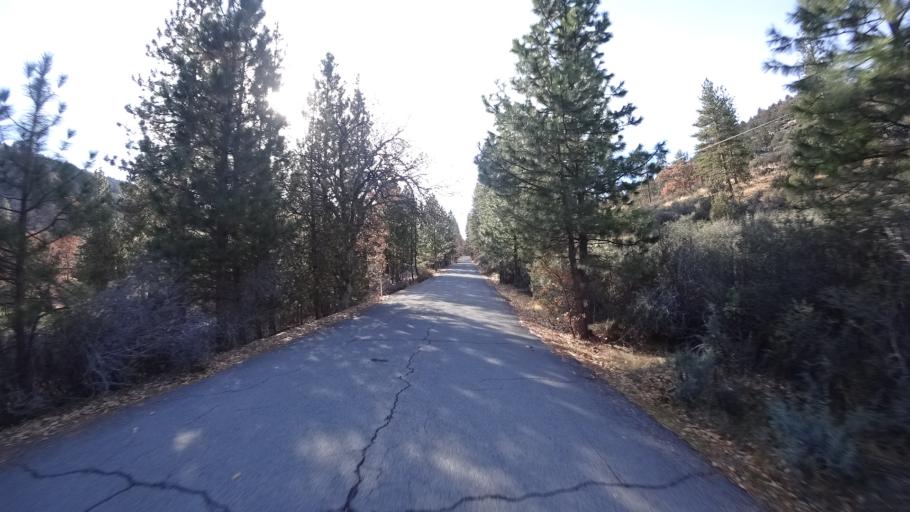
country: US
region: California
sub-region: Siskiyou County
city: Montague
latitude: 41.6093
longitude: -122.5773
